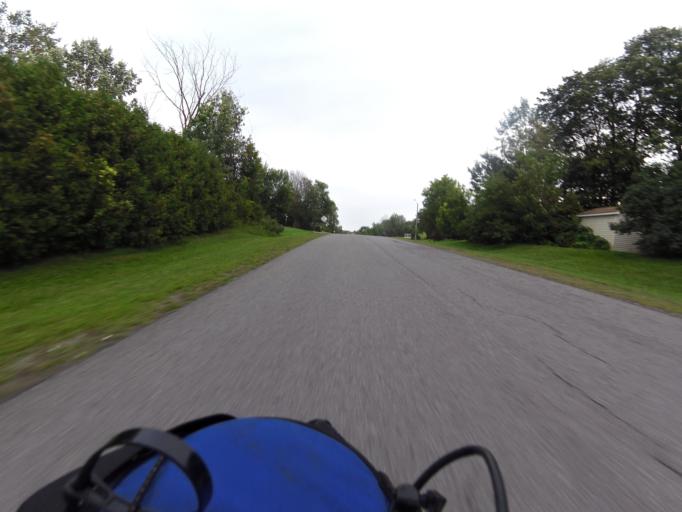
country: CA
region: Ontario
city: Ottawa
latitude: 45.2332
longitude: -75.4677
